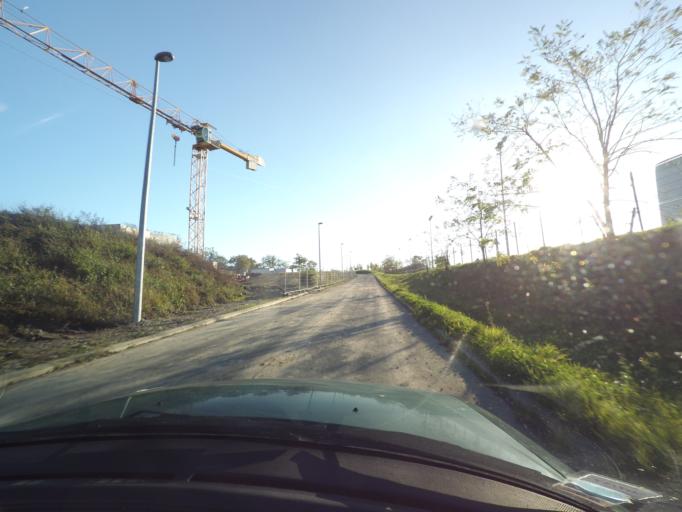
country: FR
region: Pays de la Loire
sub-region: Departement de la Loire-Atlantique
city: Le Bignon
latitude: 47.0990
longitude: -1.4491
